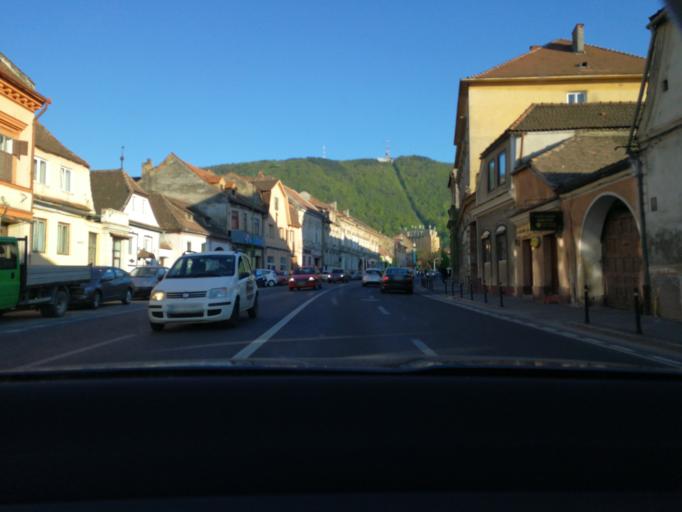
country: RO
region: Brasov
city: Brasov
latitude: 45.6491
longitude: 25.5883
